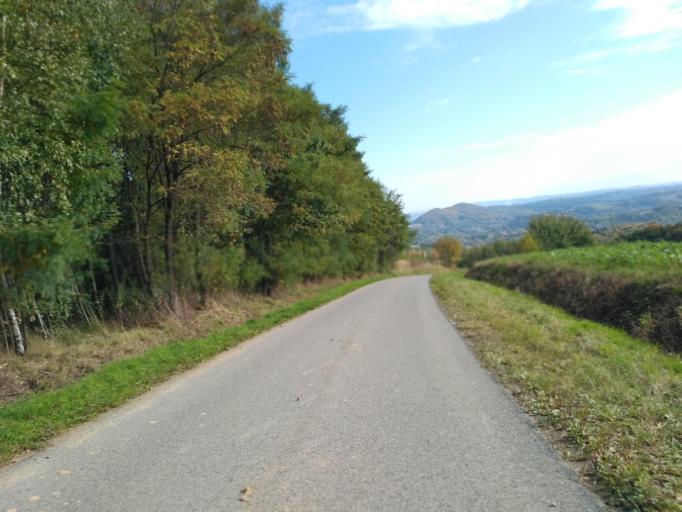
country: PL
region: Subcarpathian Voivodeship
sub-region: Powiat debicki
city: Slotowa
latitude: 49.9319
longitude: 21.2739
